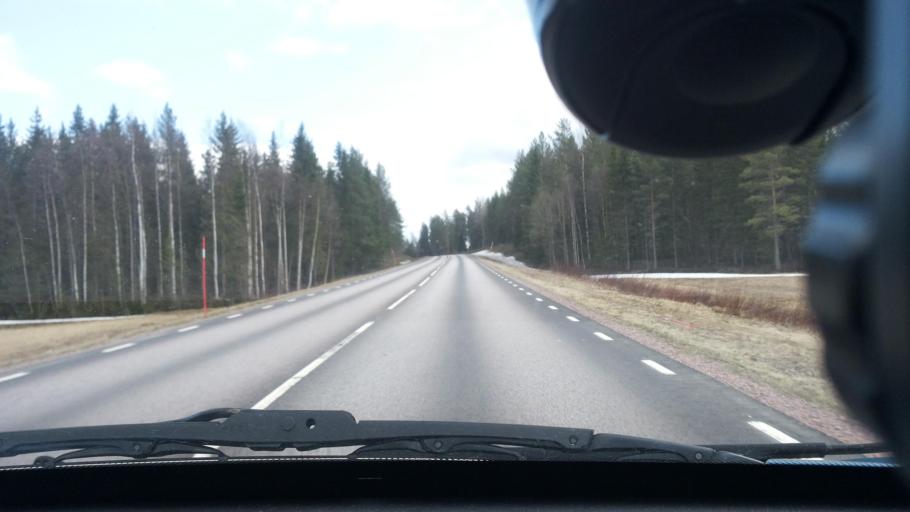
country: SE
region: Norrbotten
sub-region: Lulea Kommun
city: Sodra Sunderbyn
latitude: 65.6094
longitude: 21.9591
